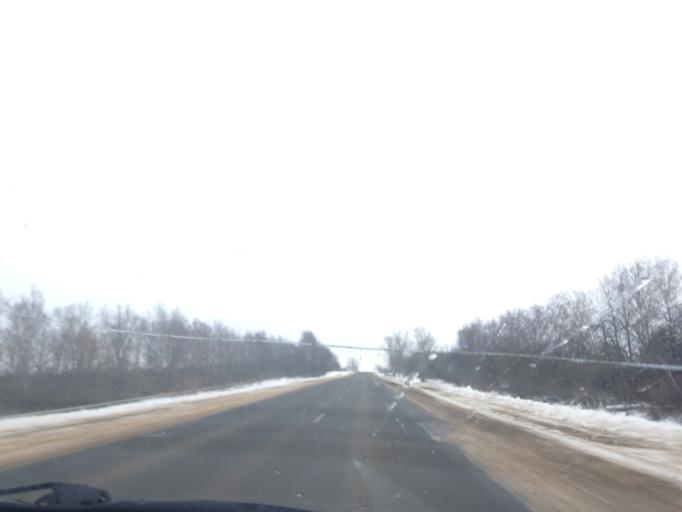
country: RU
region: Tula
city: Shchekino
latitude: 53.9697
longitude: 37.4976
